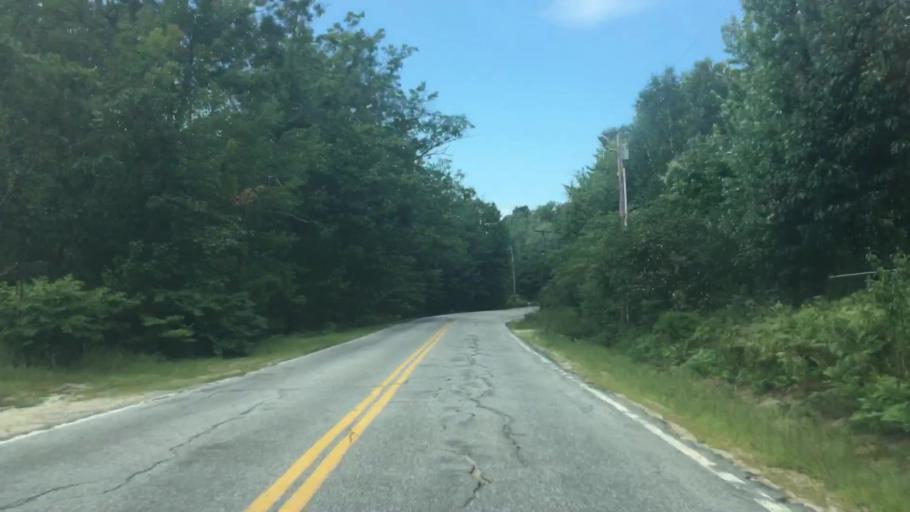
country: US
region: Maine
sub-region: Oxford County
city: Oxford
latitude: 44.0761
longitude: -70.5485
